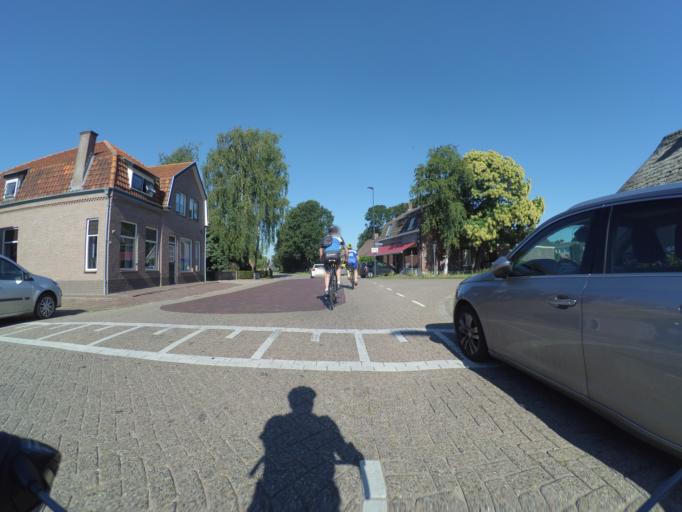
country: NL
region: North Brabant
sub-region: Gemeente Dongen
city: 's Gravenmoer
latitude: 51.6504
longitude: 4.9247
